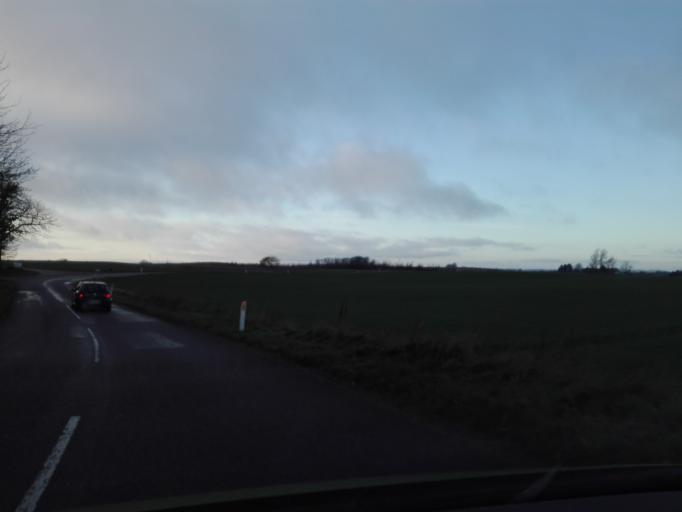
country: DK
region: Central Jutland
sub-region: Skanderborg Kommune
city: Stilling
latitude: 56.0411
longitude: 10.0065
